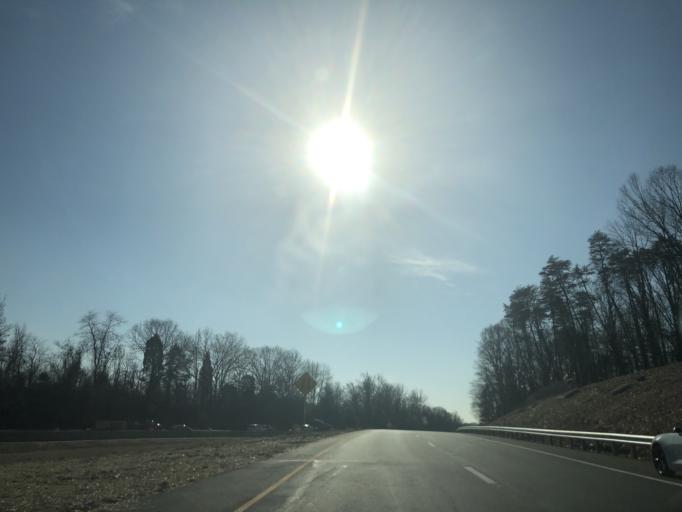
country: US
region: Virginia
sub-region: Stafford County
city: Stafford
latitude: 38.4190
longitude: -77.4254
